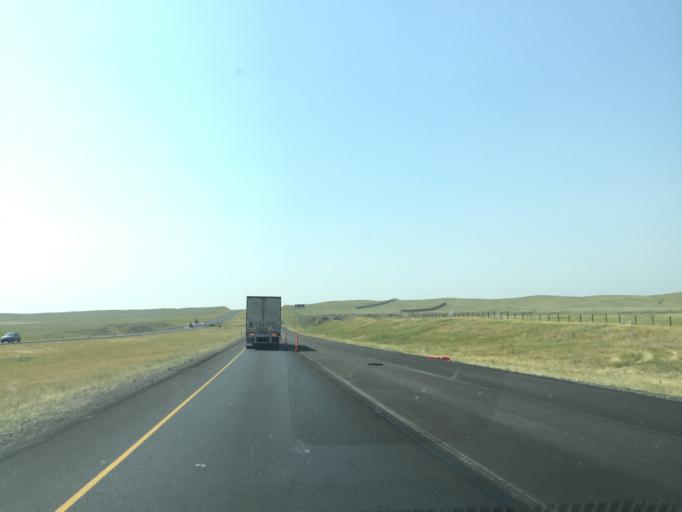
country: US
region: Wyoming
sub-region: Laramie County
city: Ranchettes
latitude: 41.3283
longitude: -104.8632
